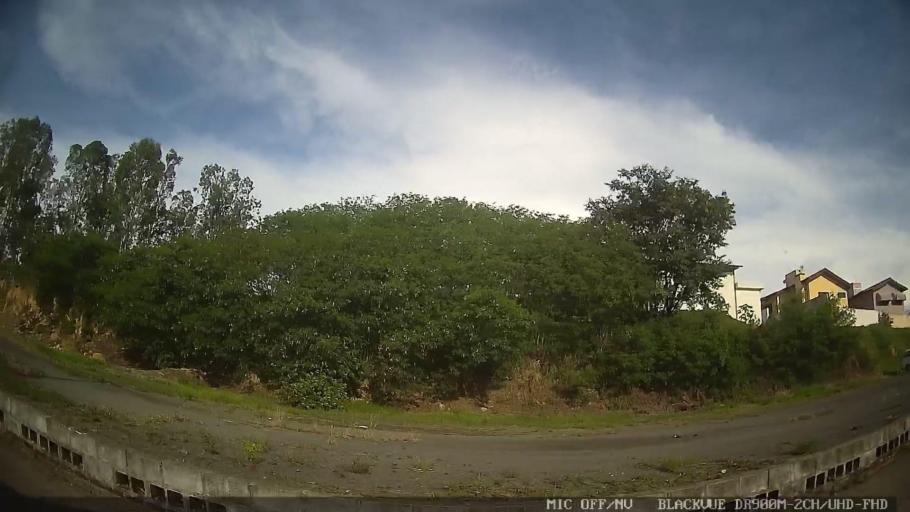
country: BR
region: Sao Paulo
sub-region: Tiete
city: Tiete
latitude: -23.1156
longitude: -47.7128
